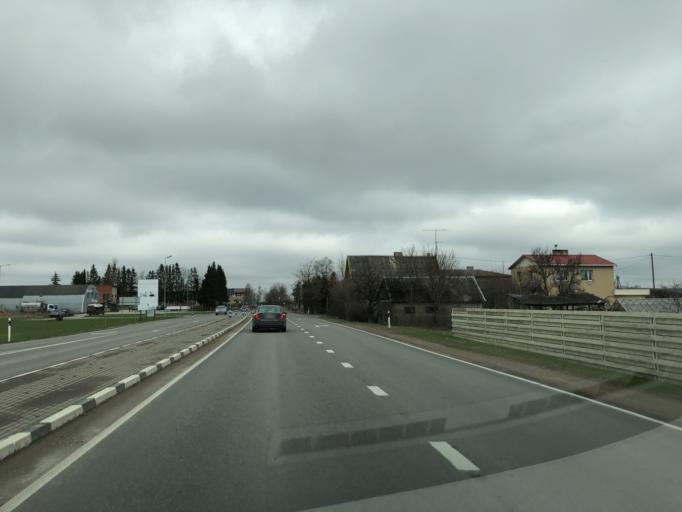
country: EE
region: Laeaene-Virumaa
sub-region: Rakvere linn
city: Rakvere
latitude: 59.3581
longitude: 26.3353
